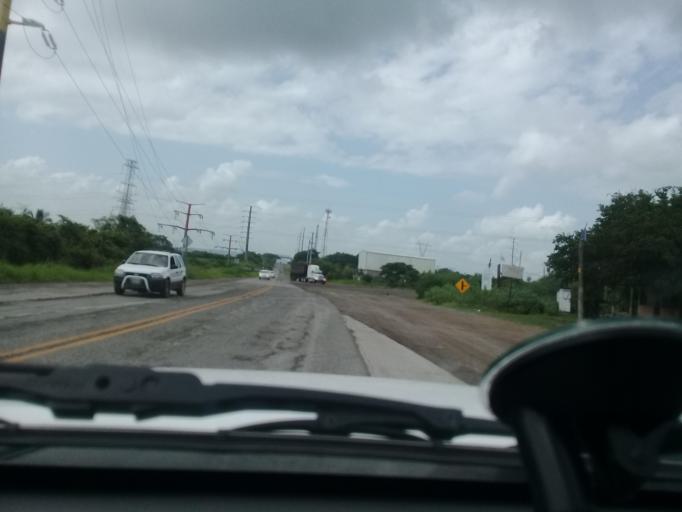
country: MX
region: Veracruz
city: Moralillo
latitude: 22.2189
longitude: -98.0006
